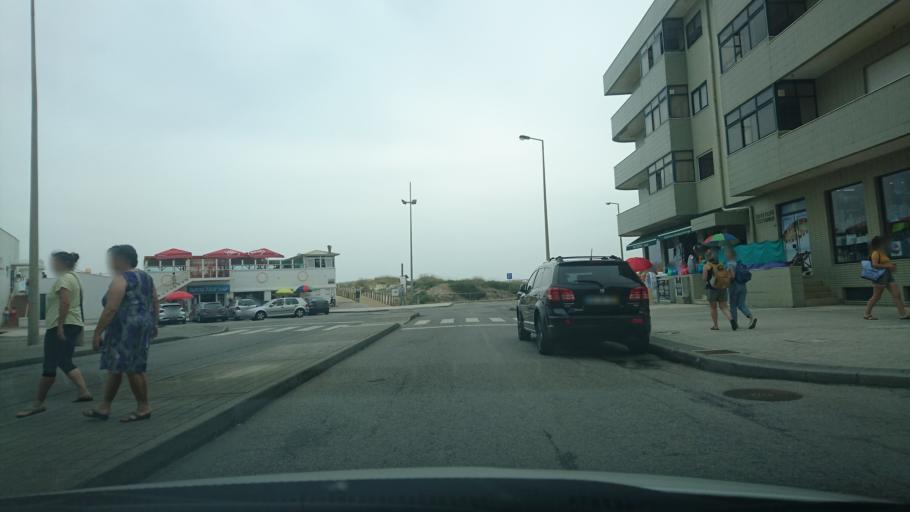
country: PT
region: Aveiro
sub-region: Ovar
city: Esmoriz
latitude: 40.9580
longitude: -8.6533
